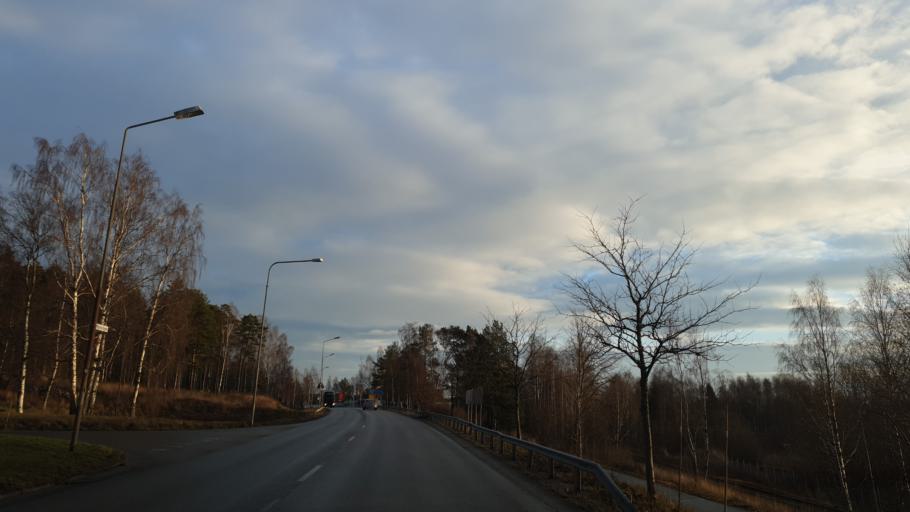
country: SE
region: Gaevleborg
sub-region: Hudiksvalls Kommun
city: Hudiksvall
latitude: 61.7242
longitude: 17.1400
